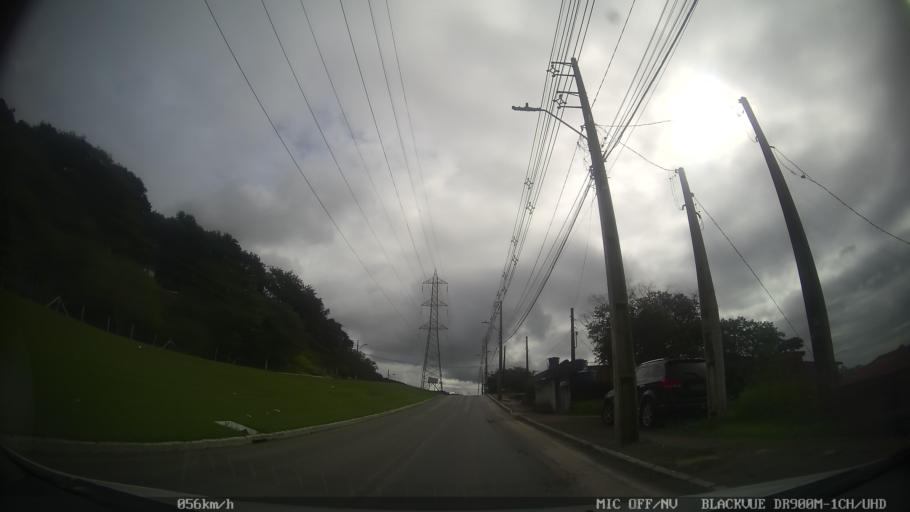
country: BR
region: Santa Catarina
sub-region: Biguacu
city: Biguacu
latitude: -27.5502
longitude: -48.6455
